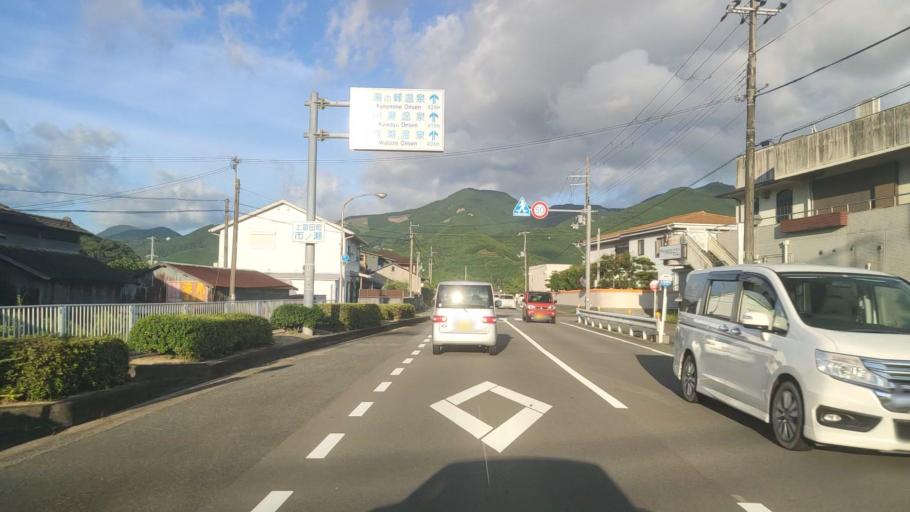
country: JP
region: Wakayama
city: Tanabe
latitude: 33.7157
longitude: 135.4639
